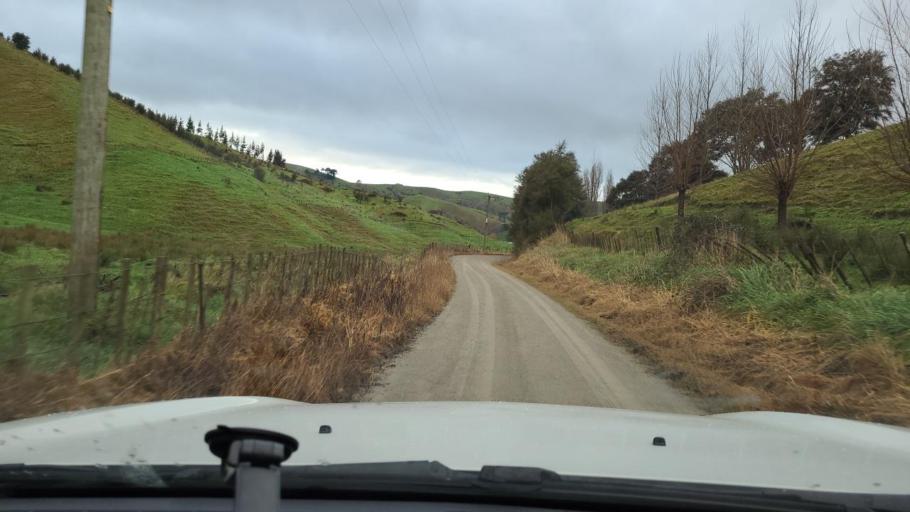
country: NZ
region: Gisborne
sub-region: Gisborne District
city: Gisborne
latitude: -38.5883
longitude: 177.8071
